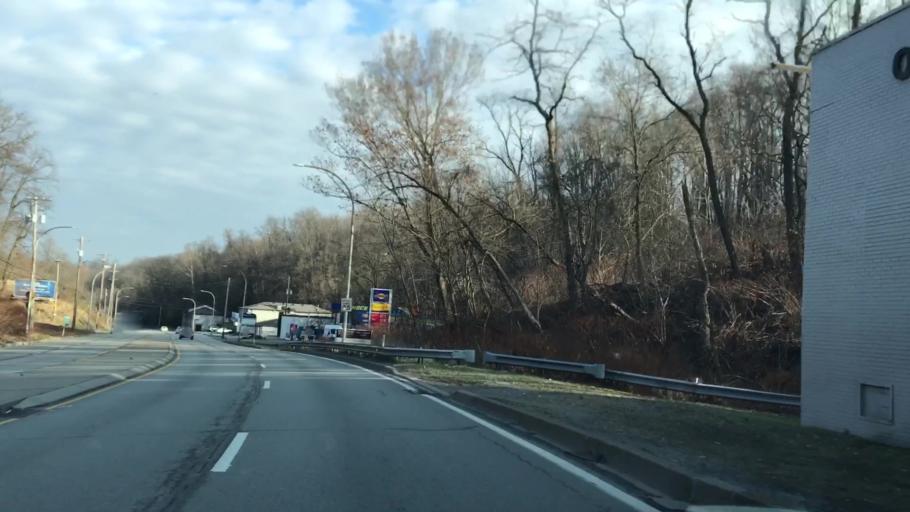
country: US
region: Pennsylvania
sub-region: Allegheny County
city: Dormont
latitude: 40.4080
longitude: -80.0328
